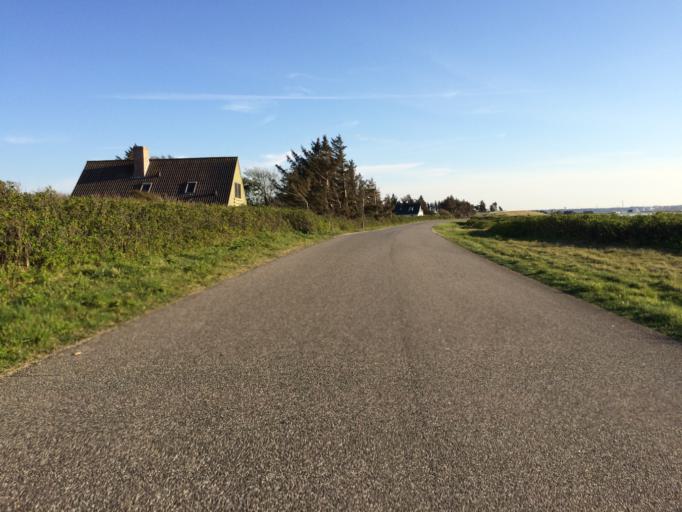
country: DK
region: Central Jutland
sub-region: Struer Kommune
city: Struer
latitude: 56.5233
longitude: 8.6295
